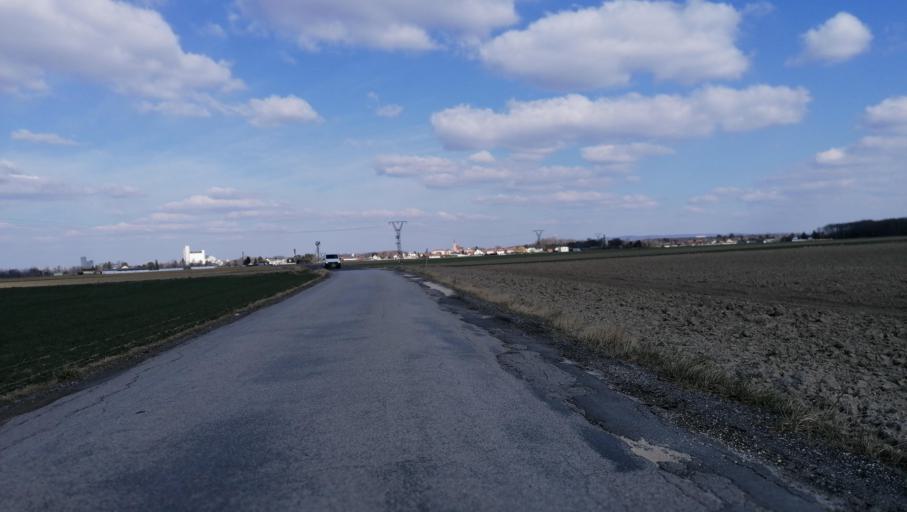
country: AT
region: Lower Austria
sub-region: Politischer Bezirk Wiener Neustadt
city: Lichtenworth
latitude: 47.8240
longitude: 16.2780
